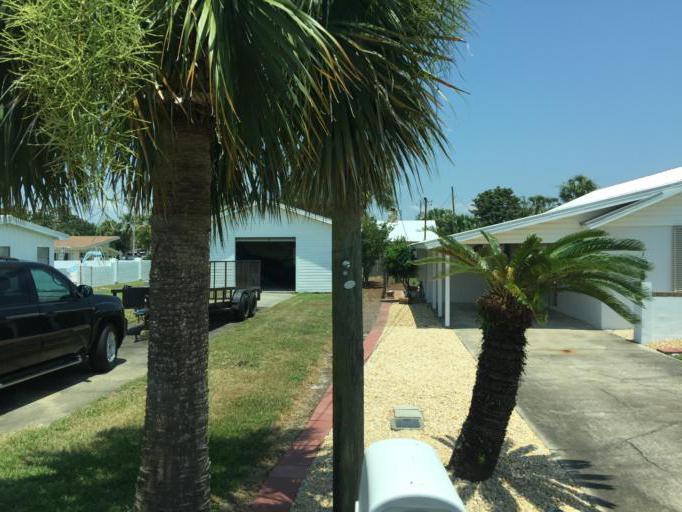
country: US
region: Florida
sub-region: Bay County
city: Panama City Beach
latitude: 30.2091
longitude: -85.8552
